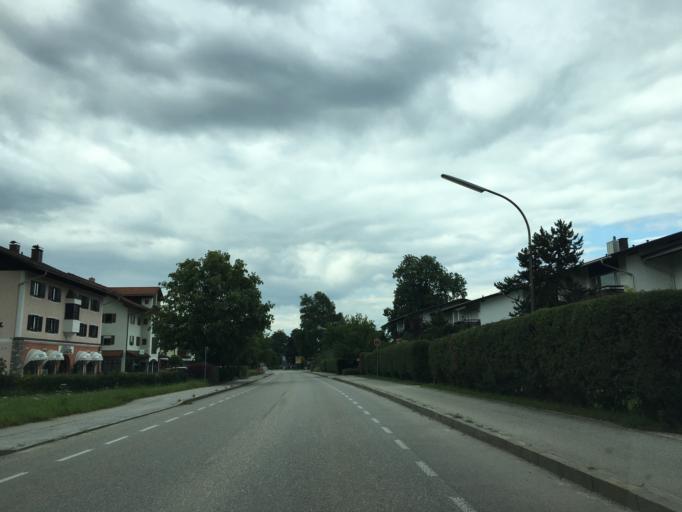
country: DE
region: Bavaria
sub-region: Upper Bavaria
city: Brannenburg
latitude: 47.7387
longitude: 12.1042
